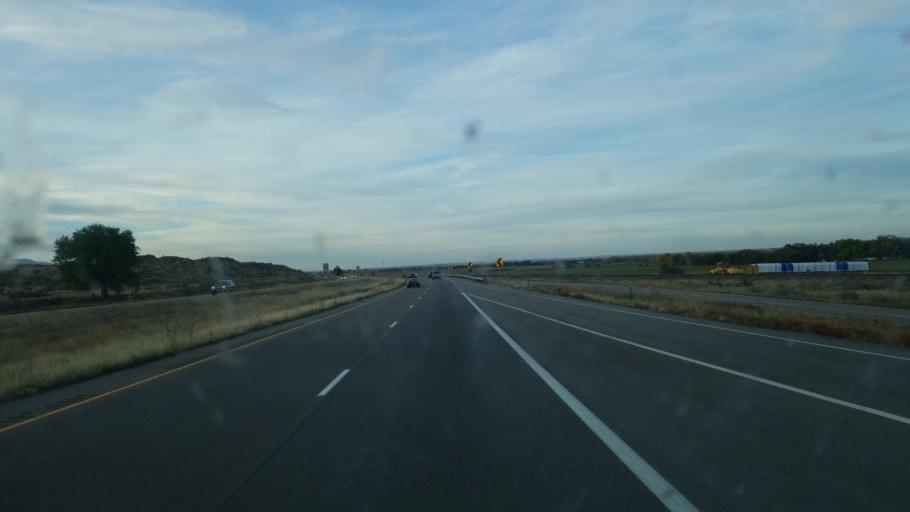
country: US
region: Colorado
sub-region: El Paso County
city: Fountain
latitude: 38.5138
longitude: -104.6290
